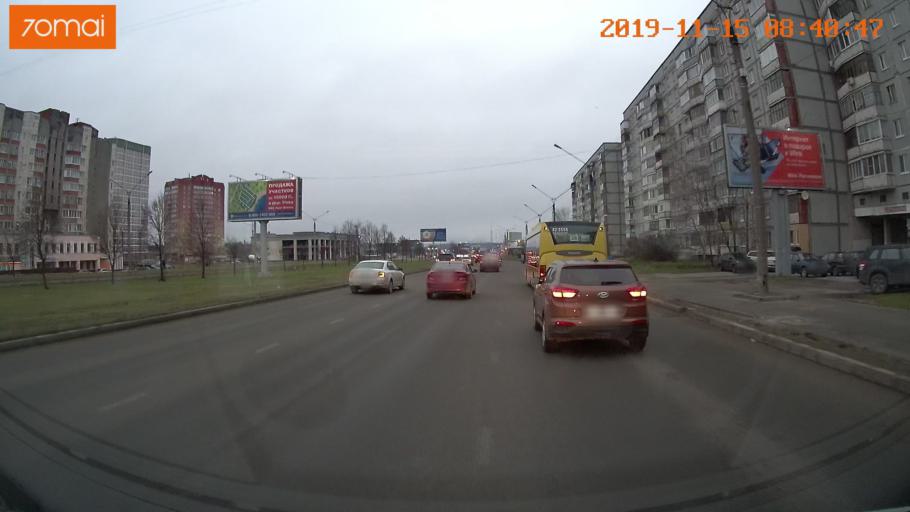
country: RU
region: Vologda
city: Cherepovets
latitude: 59.0957
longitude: 37.9133
